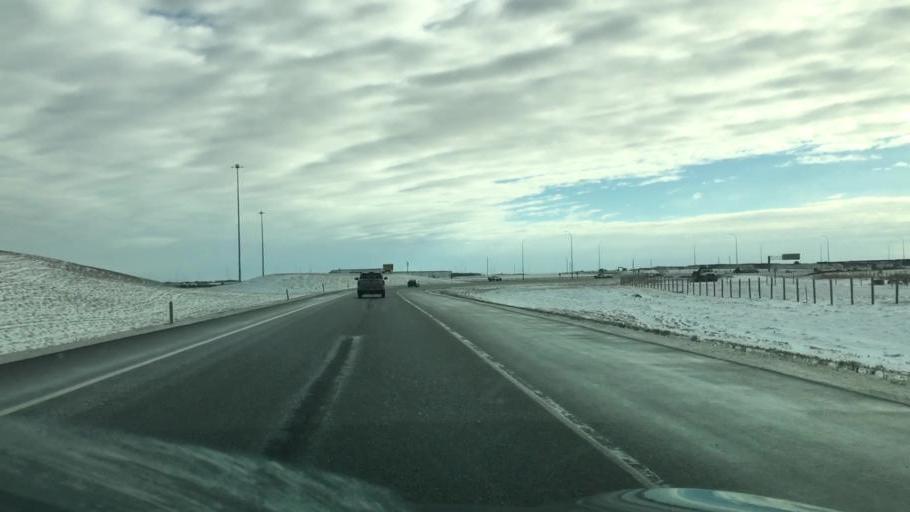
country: CA
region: Alberta
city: Airdrie
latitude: 51.1735
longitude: -114.0045
